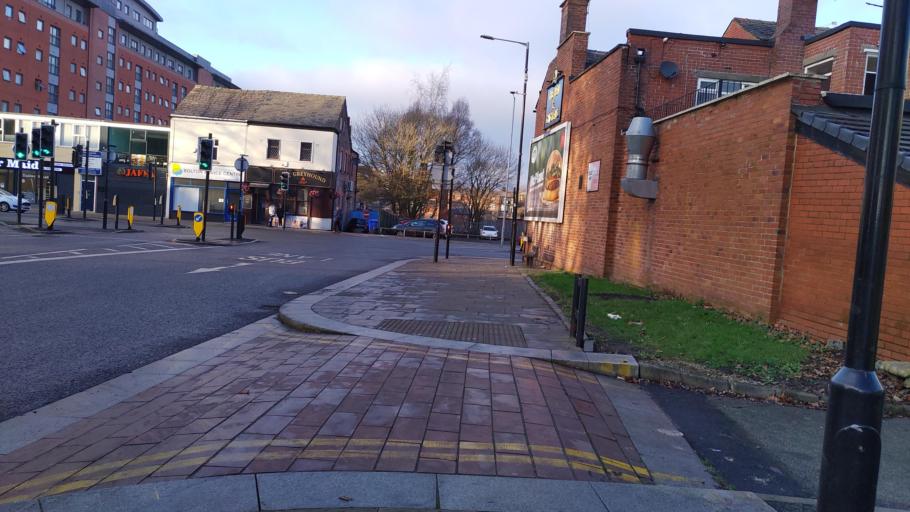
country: GB
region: England
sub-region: Borough of Bolton
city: Bolton
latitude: 53.5785
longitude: -2.4332
